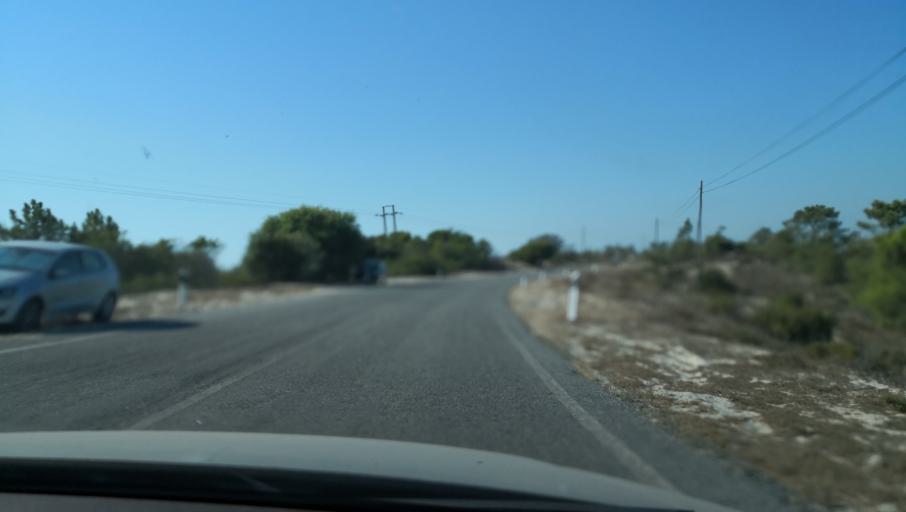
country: PT
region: Setubal
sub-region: Setubal
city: Setubal
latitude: 38.4193
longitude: -8.8196
